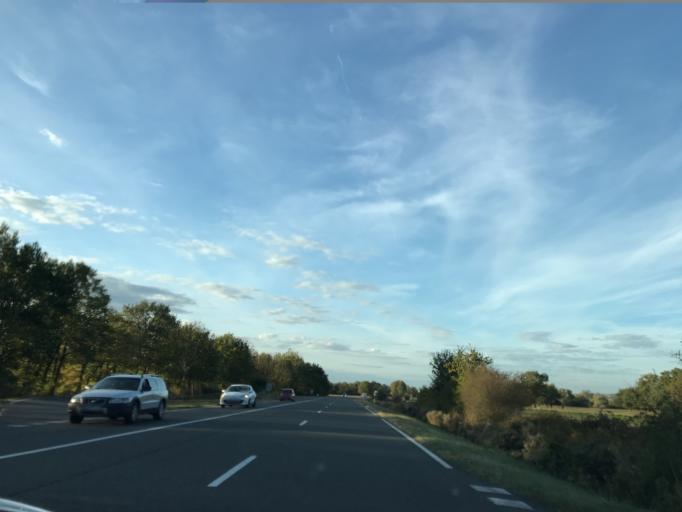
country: FR
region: Auvergne
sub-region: Departement de l'Allier
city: Saint-Yorre
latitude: 46.0210
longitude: 3.4808
